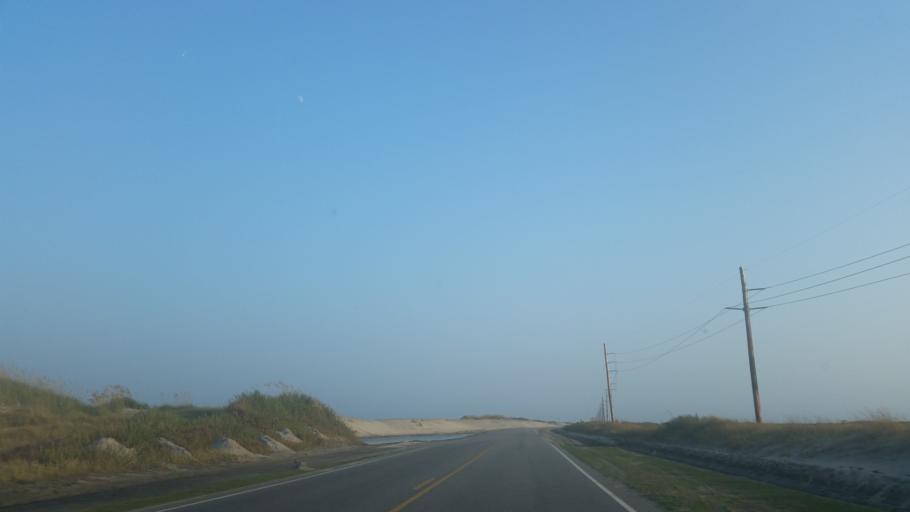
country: US
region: North Carolina
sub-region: Dare County
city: Wanchese
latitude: 35.7427
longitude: -75.5047
